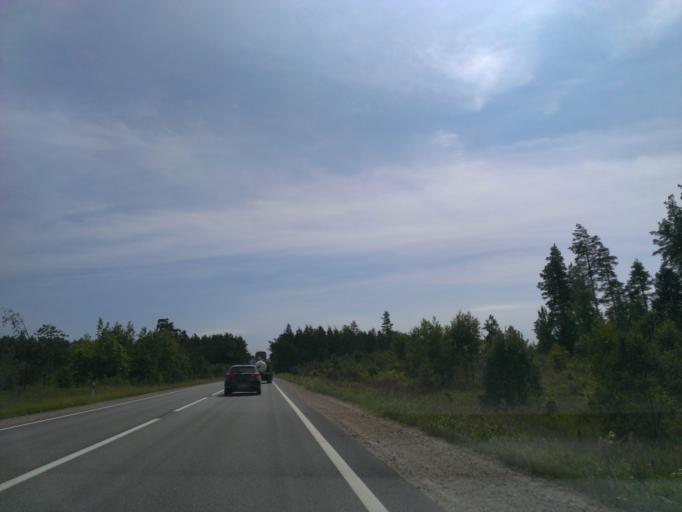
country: LV
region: Salaspils
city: Salaspils
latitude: 56.9212
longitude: 24.3947
